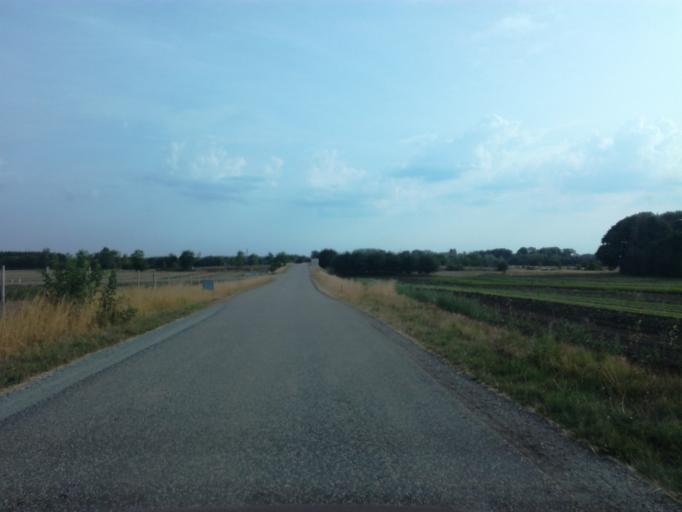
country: DK
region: South Denmark
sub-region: Vejle Kommune
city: Brejning
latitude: 55.6304
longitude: 9.6845
